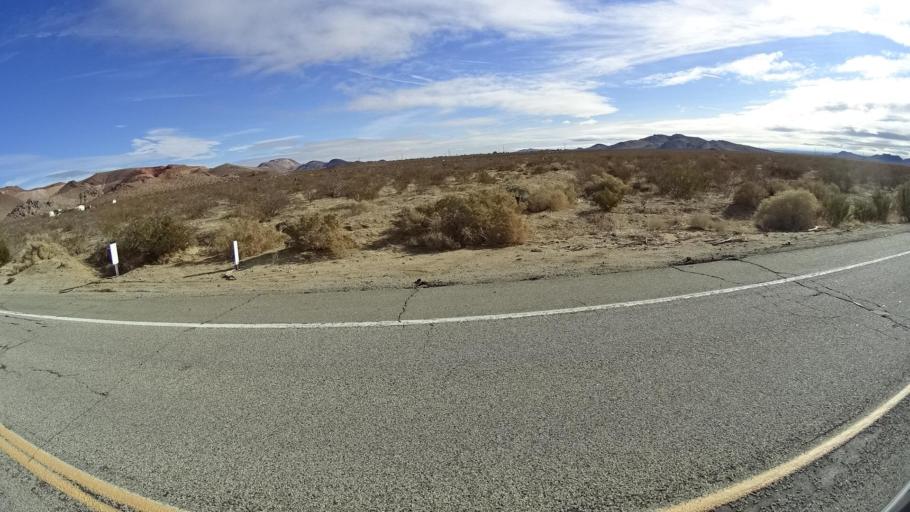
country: US
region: California
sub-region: Kern County
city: Rosamond
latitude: 34.9442
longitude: -118.2917
